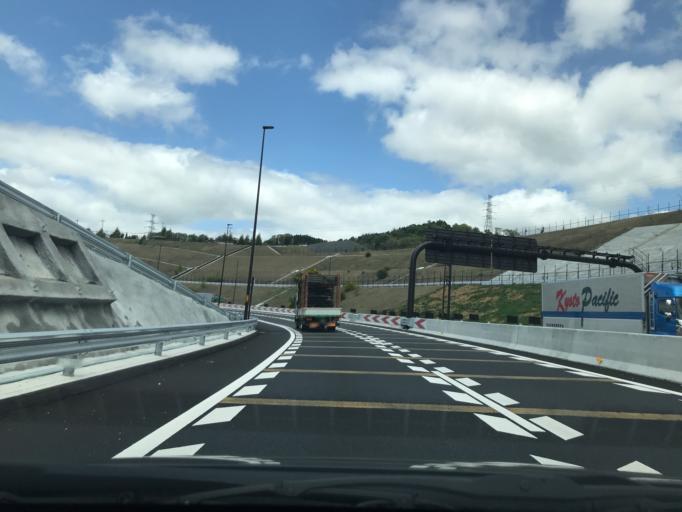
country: JP
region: Osaka
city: Takatsuki
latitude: 34.8835
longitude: 135.6258
